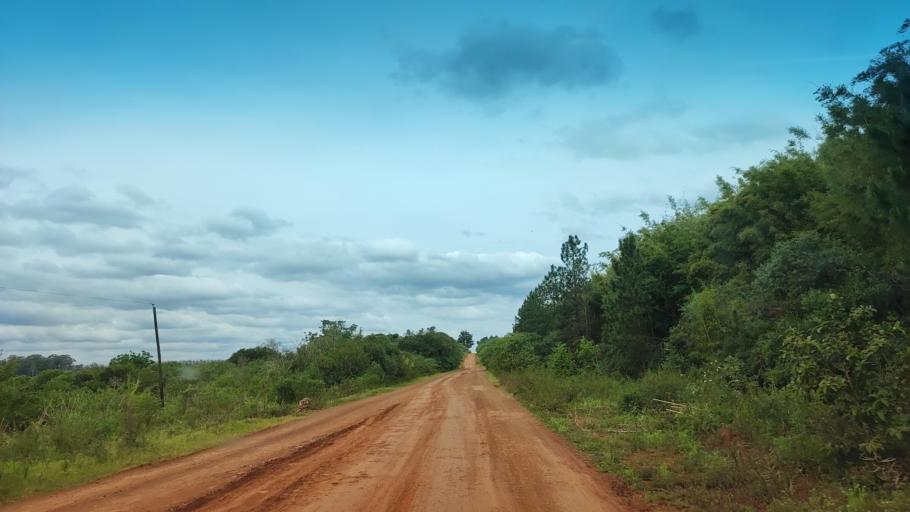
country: AR
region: Misiones
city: Garupa
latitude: -27.5187
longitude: -55.9747
